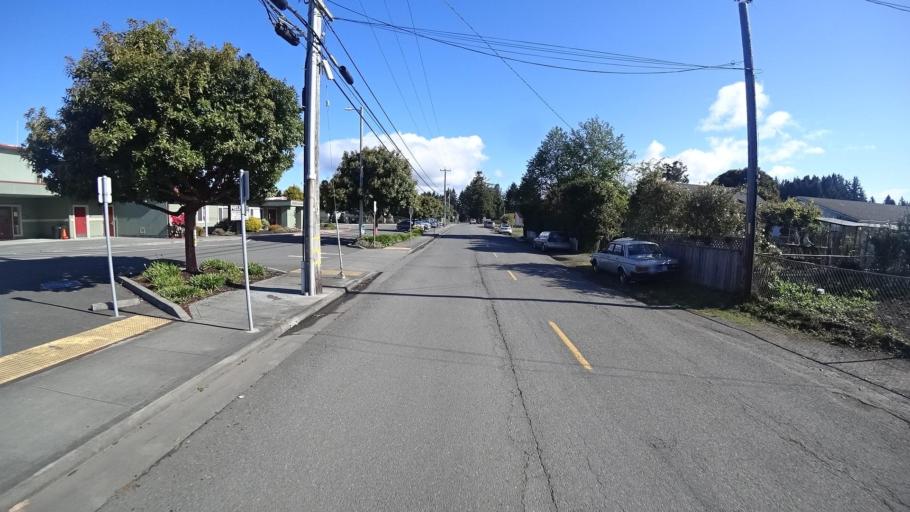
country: US
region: California
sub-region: Humboldt County
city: McKinleyville
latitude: 40.9766
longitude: -124.0959
